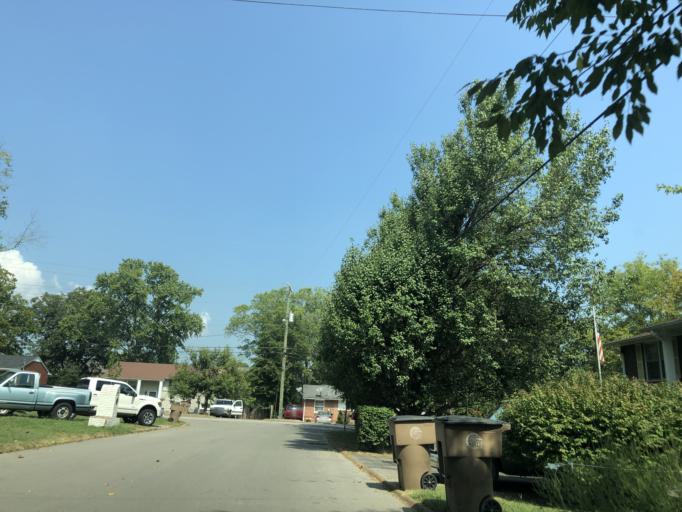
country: US
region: Tennessee
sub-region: Davidson County
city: Lakewood
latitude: 36.1573
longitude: -86.6420
